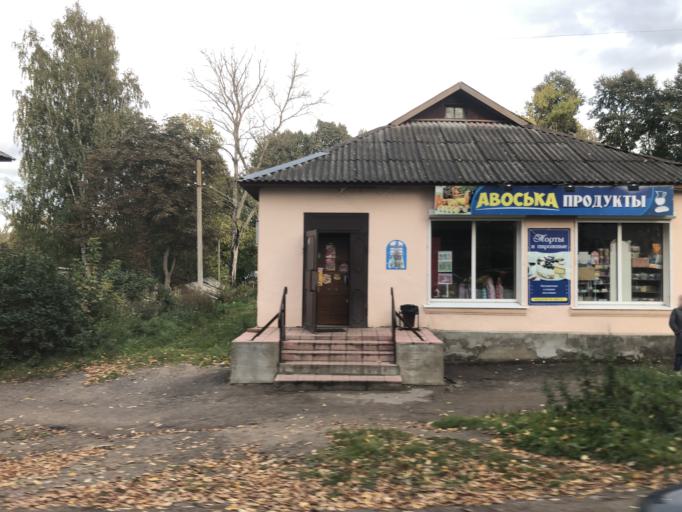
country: RU
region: Tverskaya
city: Rzhev
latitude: 56.2519
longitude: 34.2930
